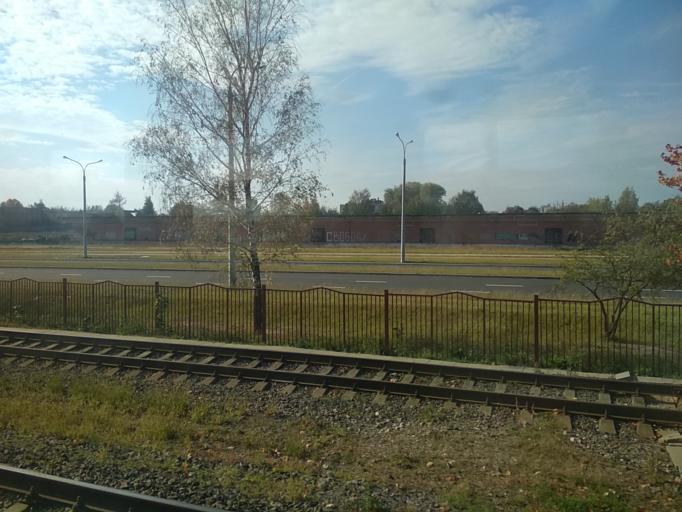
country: BY
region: Minsk
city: Minsk
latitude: 53.8639
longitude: 27.5600
